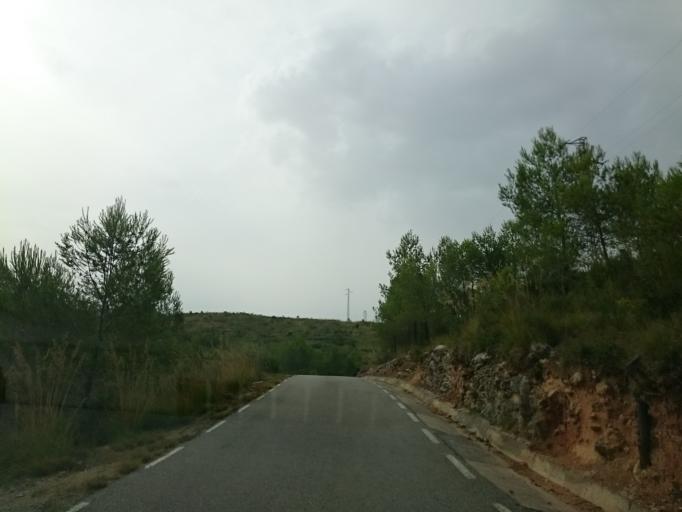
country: ES
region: Catalonia
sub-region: Provincia de Barcelona
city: Olivella
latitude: 41.3031
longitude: 1.8460
